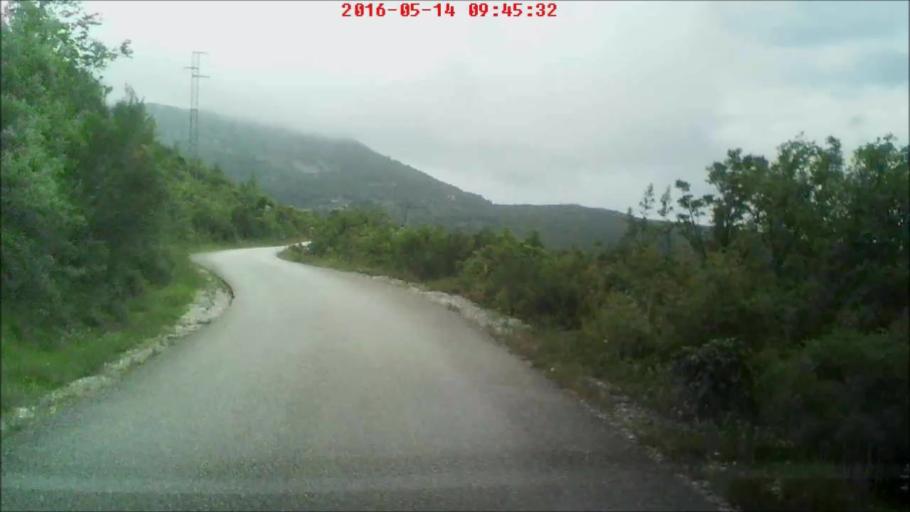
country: HR
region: Dubrovacko-Neretvanska
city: Podgora
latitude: 42.7817
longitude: 17.9118
